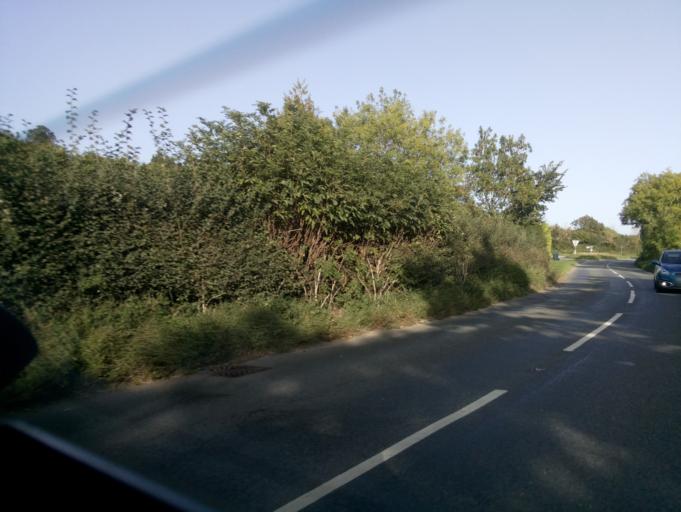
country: GB
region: England
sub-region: Gloucestershire
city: Tewkesbury
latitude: 51.9450
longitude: -2.2116
